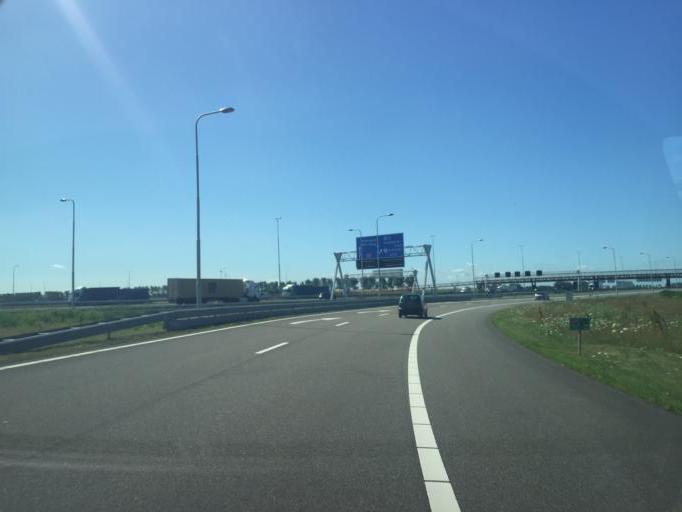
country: NL
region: North Holland
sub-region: Gemeente Haarlemmermeer
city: Hoofddorp
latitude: 52.2830
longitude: 4.7173
